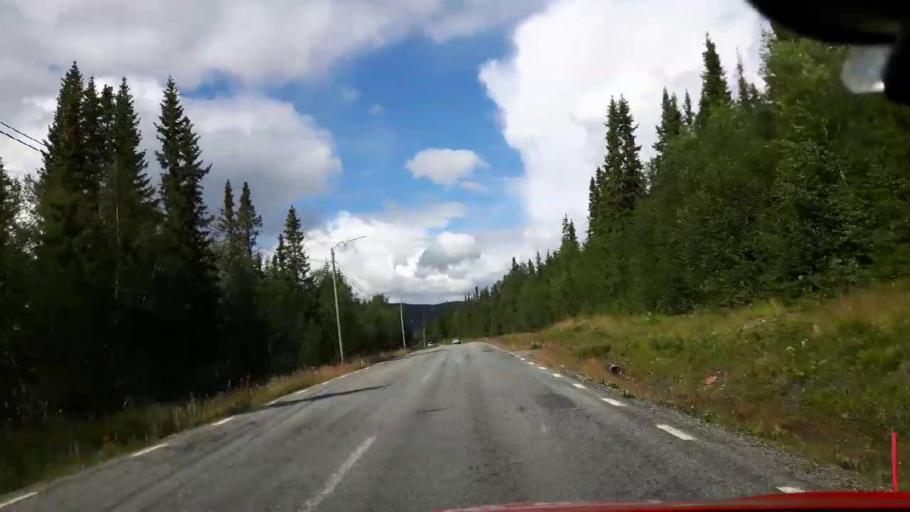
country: NO
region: Nordland
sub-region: Hattfjelldal
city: Hattfjelldal
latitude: 65.0627
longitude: 14.8736
